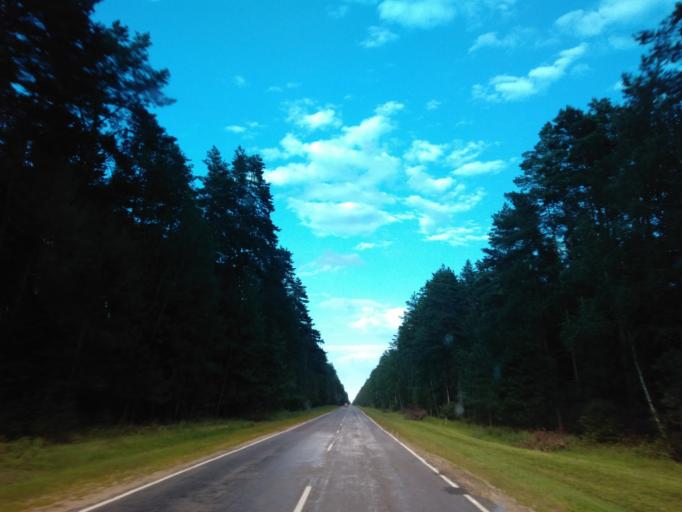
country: BY
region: Minsk
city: Uzda
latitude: 53.4215
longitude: 27.4265
